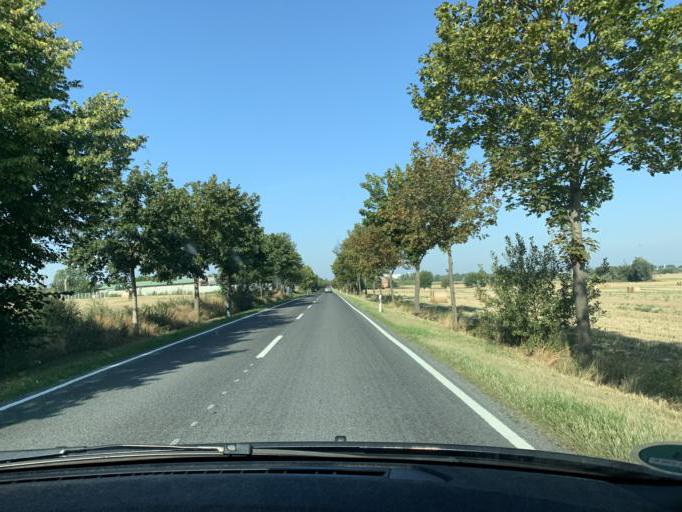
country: DE
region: Brandenburg
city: Gransee
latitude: 53.0014
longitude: 13.1973
